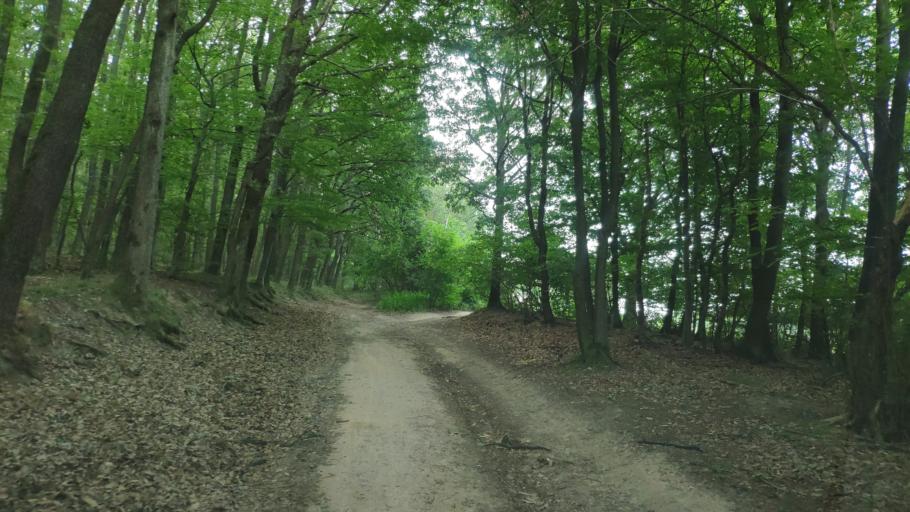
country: SK
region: Kosicky
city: Moldava nad Bodvou
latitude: 48.7173
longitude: 21.0011
